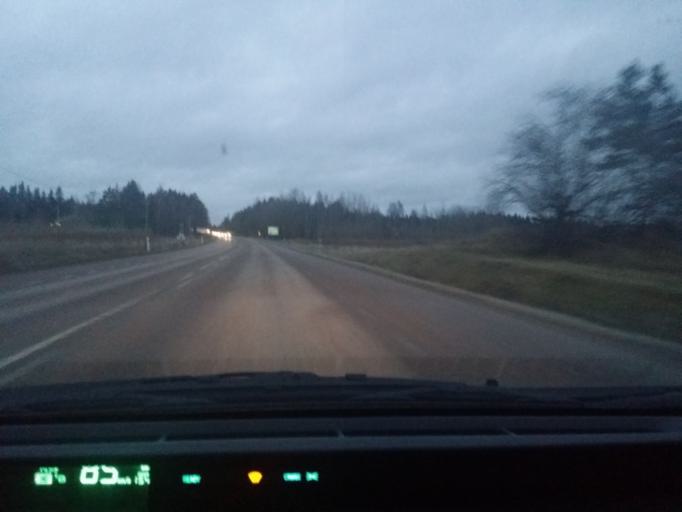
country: SE
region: Vaestmanland
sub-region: Hallstahammars Kommun
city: Kolback
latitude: 59.5737
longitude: 16.3522
